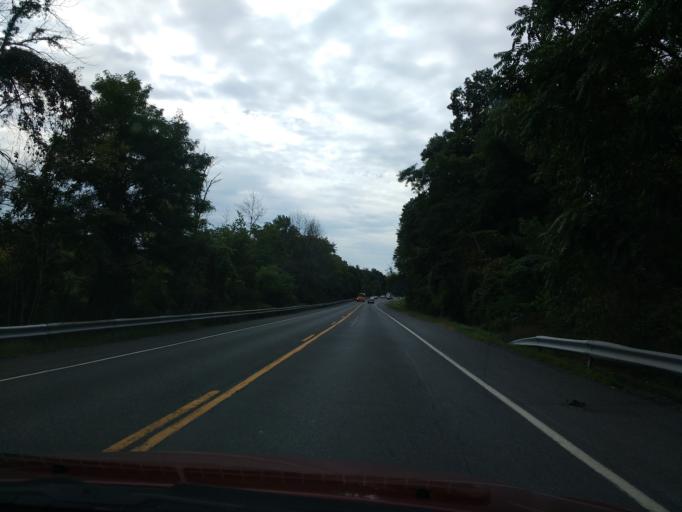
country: US
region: New York
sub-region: Ulster County
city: Lincoln Park
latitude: 41.9485
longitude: -73.9799
